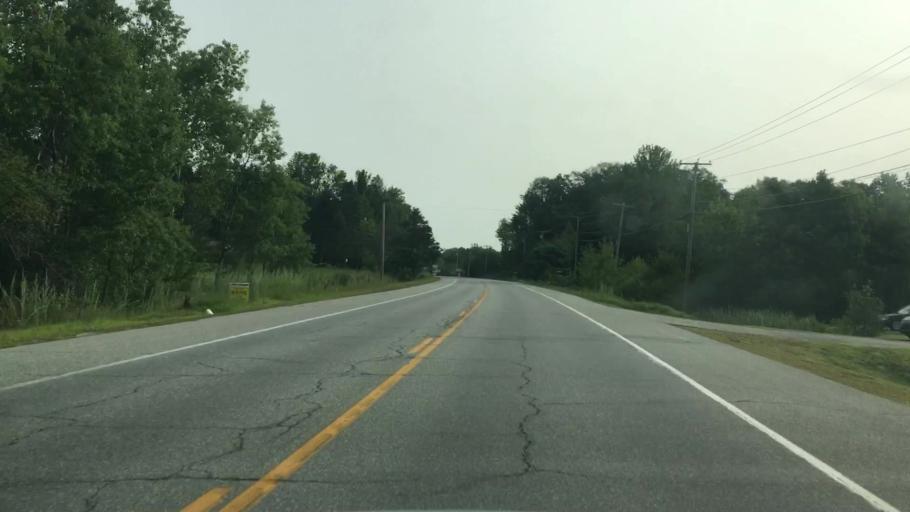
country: US
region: Maine
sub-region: Kennebec County
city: Gardiner
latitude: 44.2051
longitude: -69.7915
